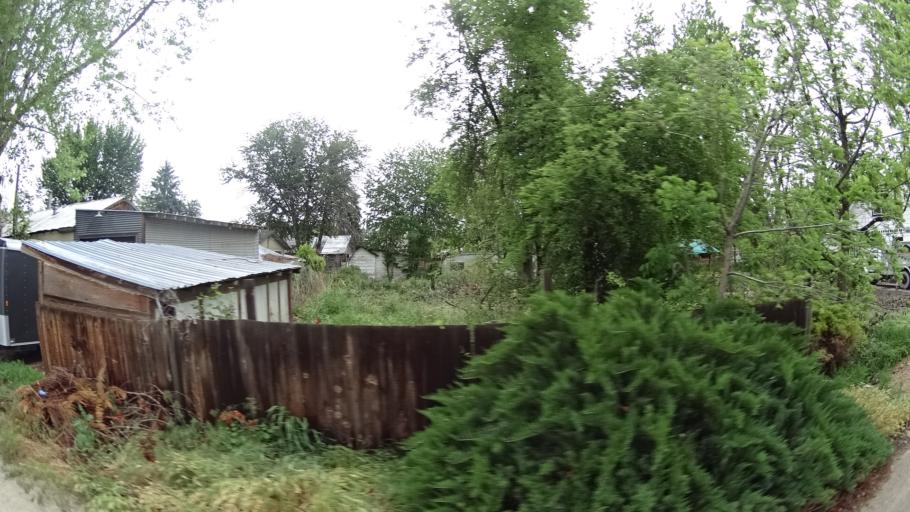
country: US
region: Idaho
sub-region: Ada County
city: Star
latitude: 43.6934
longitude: -116.4955
